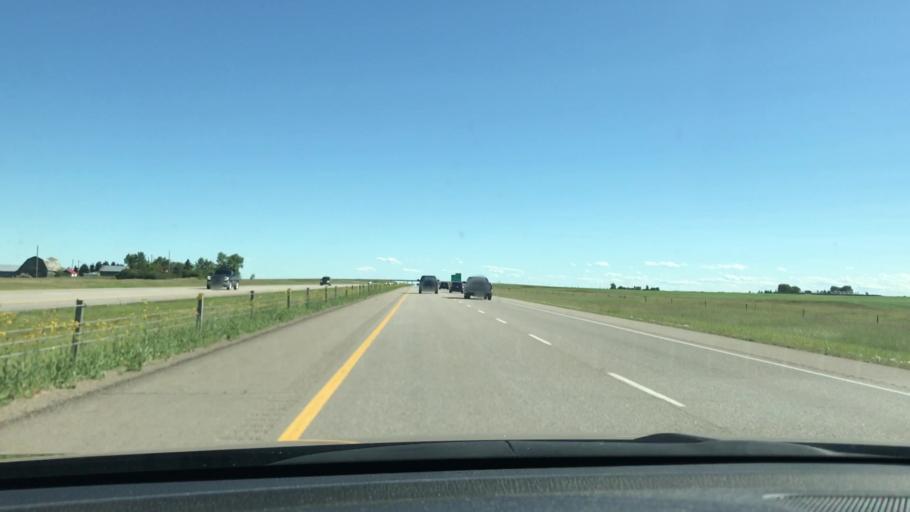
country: CA
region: Alberta
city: Didsbury
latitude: 51.6777
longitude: -114.0255
